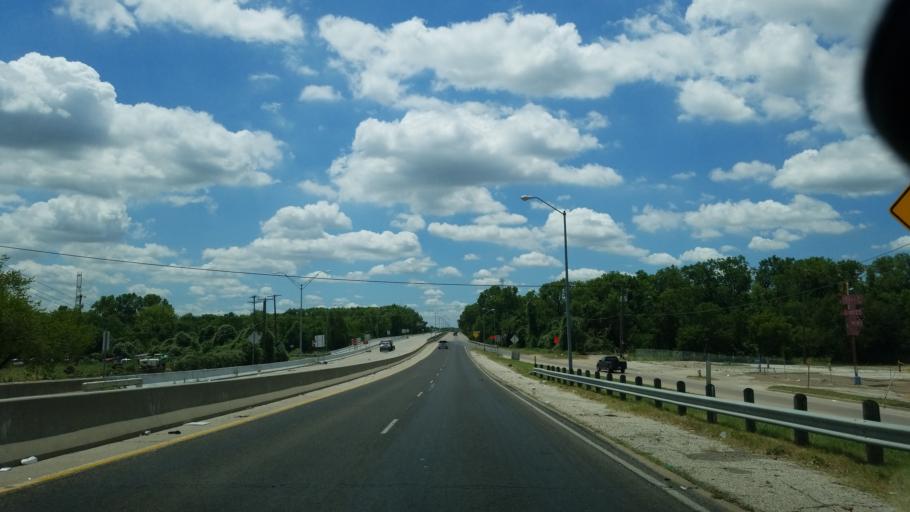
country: US
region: Texas
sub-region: Dallas County
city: Dallas
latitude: 32.7348
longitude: -96.7578
